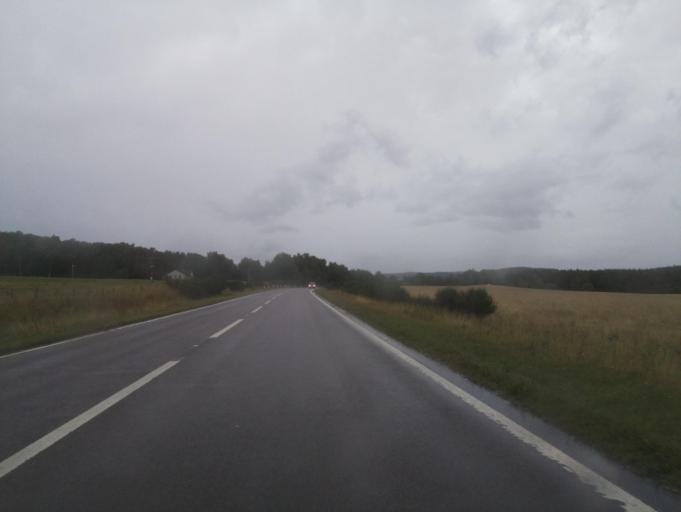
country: GB
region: Scotland
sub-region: Highland
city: Grantown on Spey
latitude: 57.2787
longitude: -3.7113
